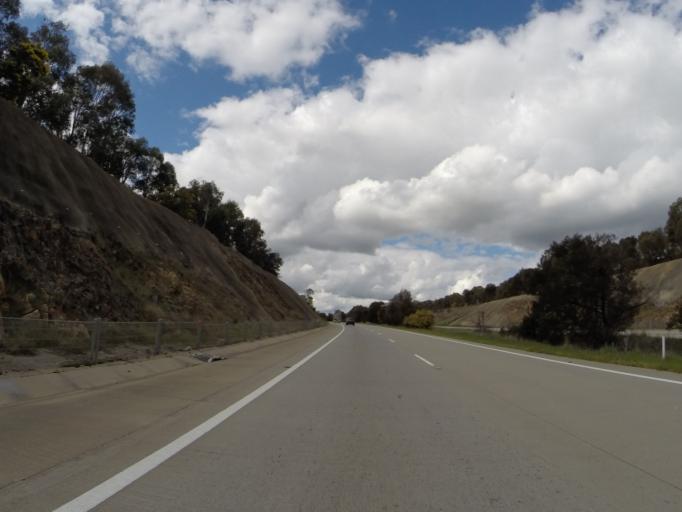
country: AU
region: New South Wales
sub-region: Yass Valley
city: Murrumbateman
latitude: -34.8010
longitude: 149.1530
